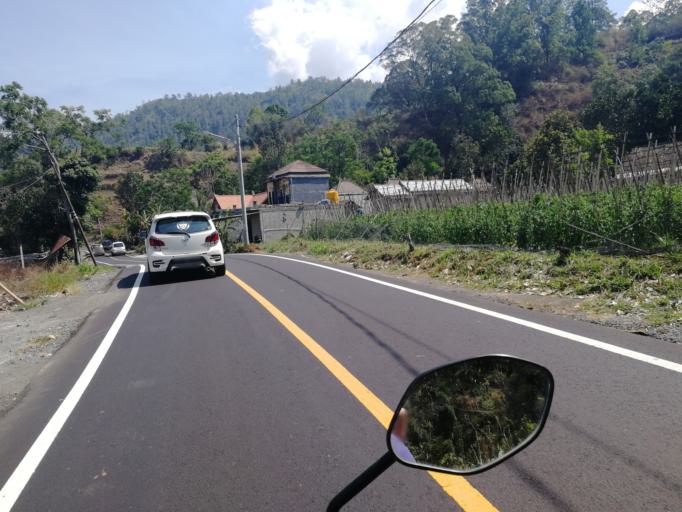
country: ID
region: Bali
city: Banjar Kedisan
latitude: -8.2757
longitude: 115.3770
